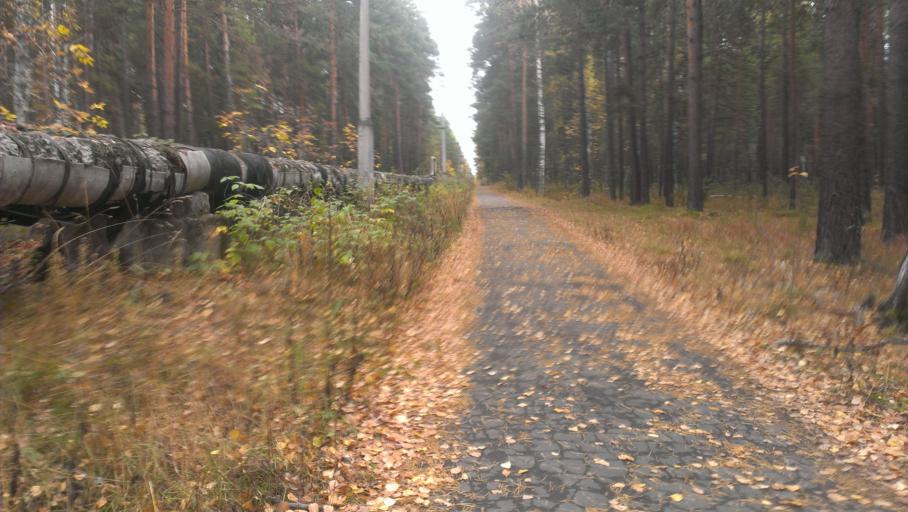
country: RU
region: Altai Krai
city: Yuzhnyy
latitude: 53.2674
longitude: 83.6832
